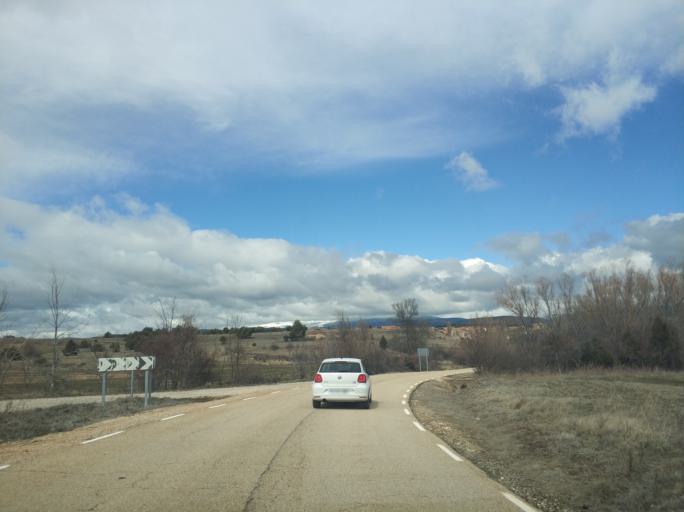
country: ES
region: Castille and Leon
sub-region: Provincia de Soria
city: Abejar
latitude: 41.7998
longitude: -2.7814
